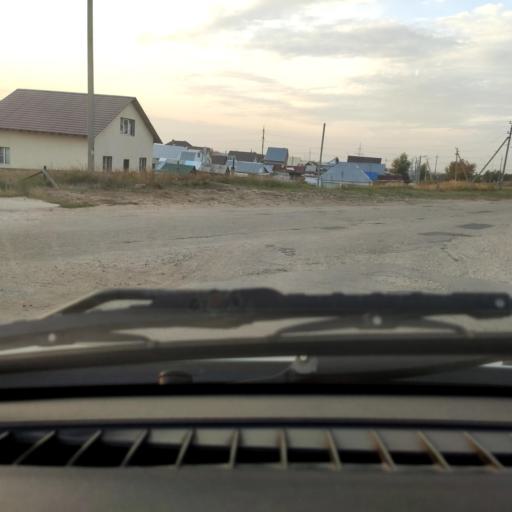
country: RU
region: Samara
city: Zhigulevsk
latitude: 53.4842
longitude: 49.5388
